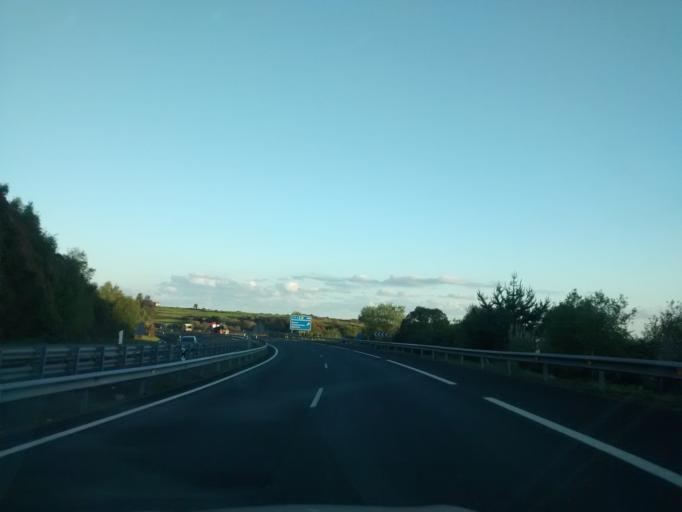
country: ES
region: Asturias
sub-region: Province of Asturias
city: Llanes
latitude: 43.4402
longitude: -4.8732
